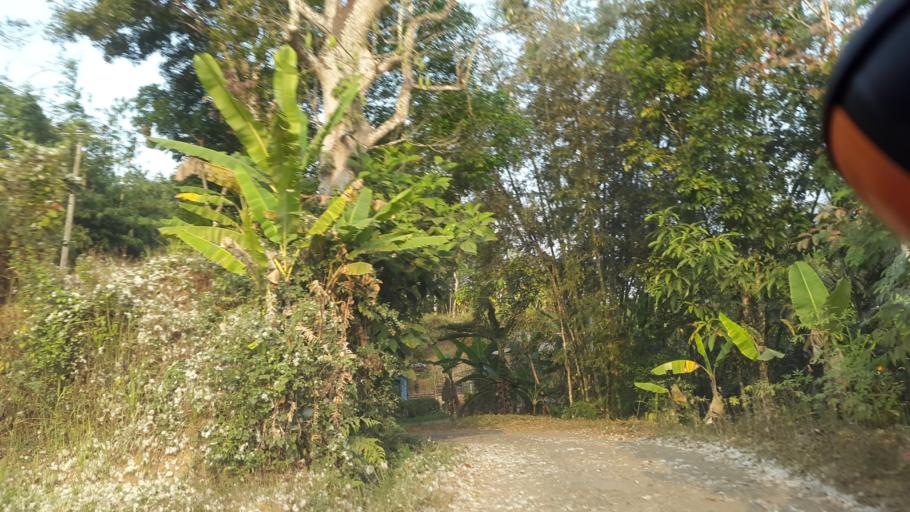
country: ID
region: West Java
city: Curugkembar Satu
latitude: -7.2080
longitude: 106.9355
